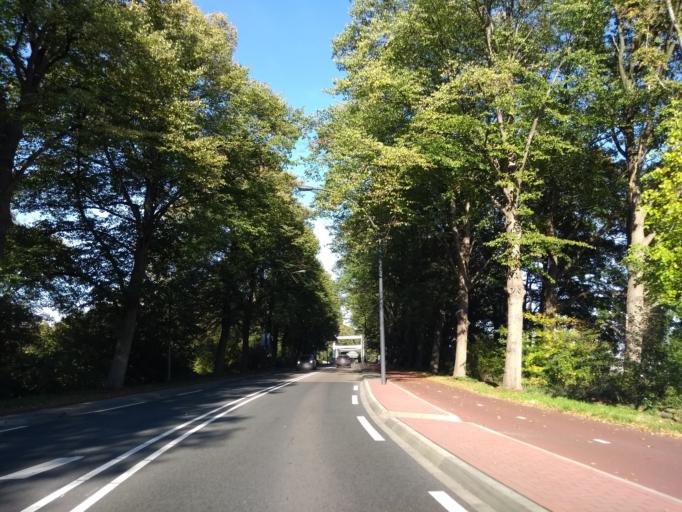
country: NL
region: Overijssel
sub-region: Gemeente Hengelo
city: Hengelo
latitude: 52.2487
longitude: 6.7660
